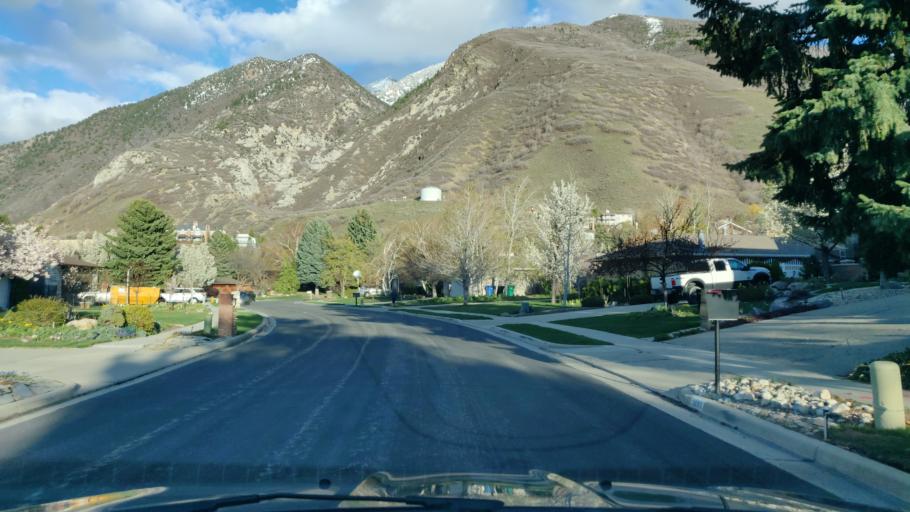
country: US
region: Utah
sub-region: Salt Lake County
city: Cottonwood Heights
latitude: 40.6147
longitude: -111.7916
